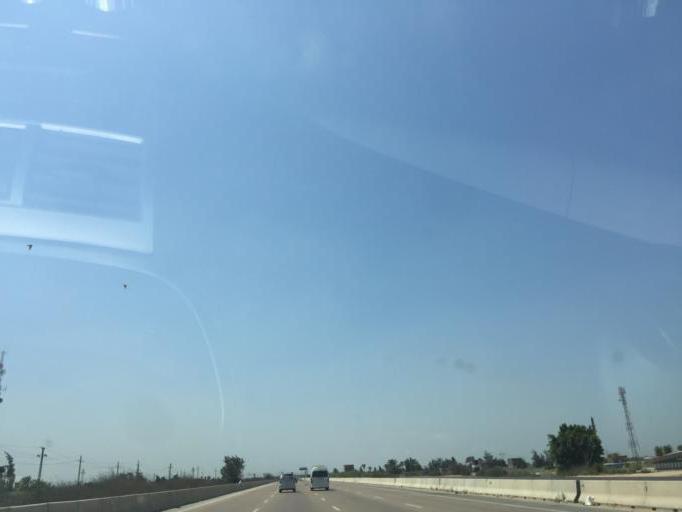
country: EG
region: Al Buhayrah
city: Abu al Matamir
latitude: 30.7770
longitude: 29.9685
